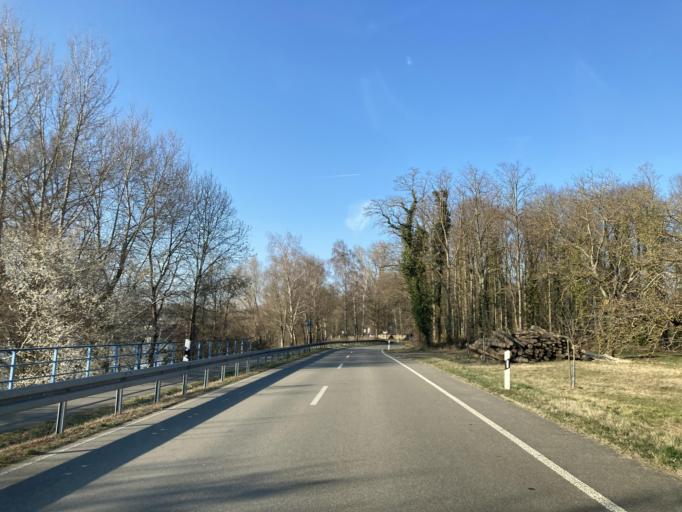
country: DE
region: Baden-Wuerttemberg
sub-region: Freiburg Region
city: Sasbach
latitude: 48.1506
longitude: 7.6006
